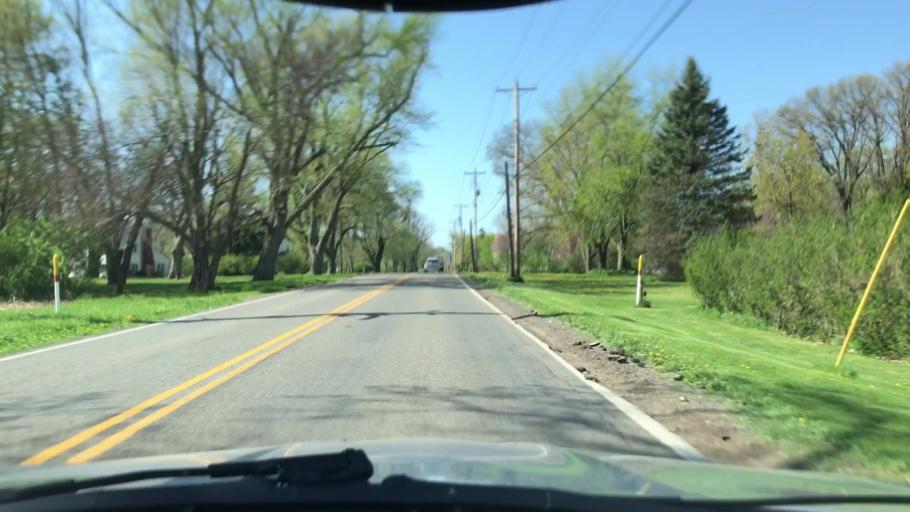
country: US
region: Indiana
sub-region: Saint Joseph County
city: Georgetown
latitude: 41.7479
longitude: -86.2993
